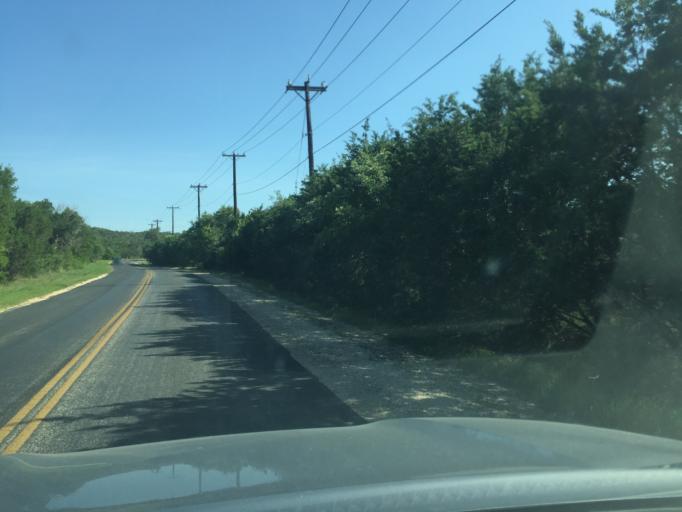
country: US
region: Texas
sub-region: Comal County
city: Bulverde
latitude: 29.7205
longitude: -98.4537
